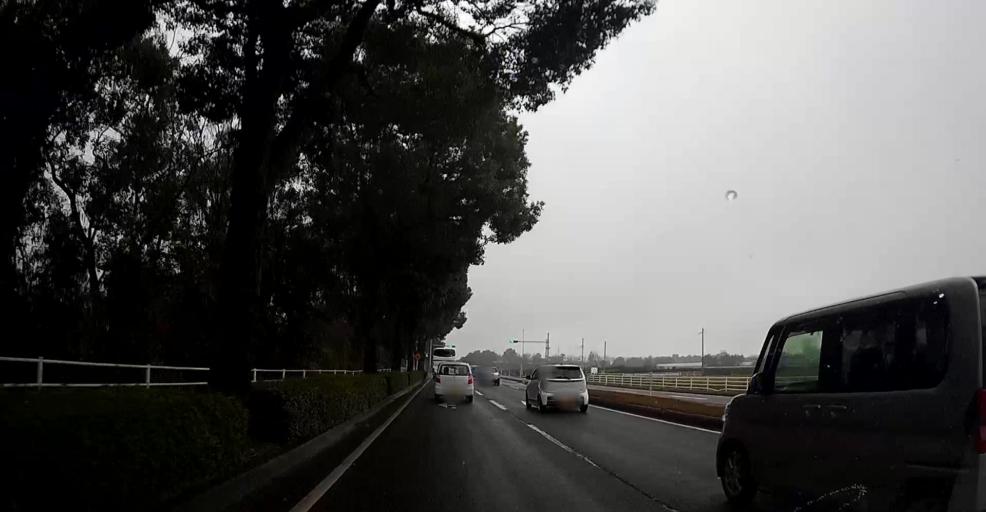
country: JP
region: Kumamoto
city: Ozu
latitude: 32.8225
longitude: 130.8531
